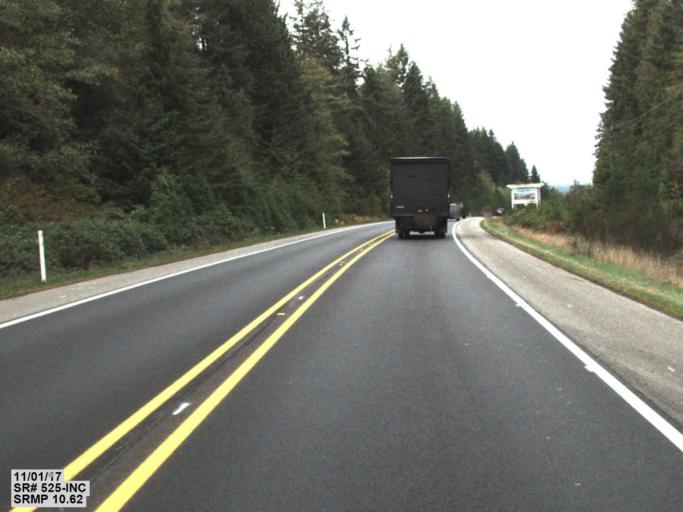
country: US
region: Washington
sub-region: Island County
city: Langley
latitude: 47.9855
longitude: -122.3908
